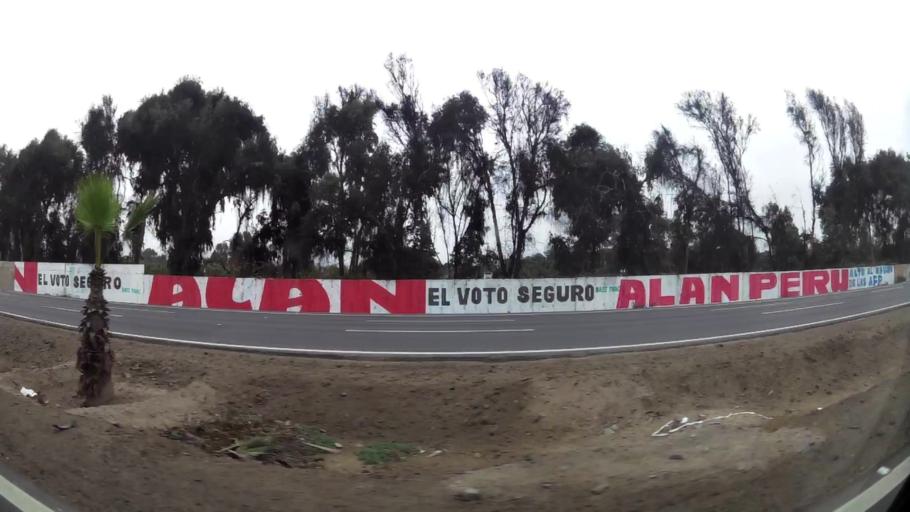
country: PE
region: Lima
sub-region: Lima
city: Punta Hermosa
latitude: -12.2621
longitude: -76.9118
